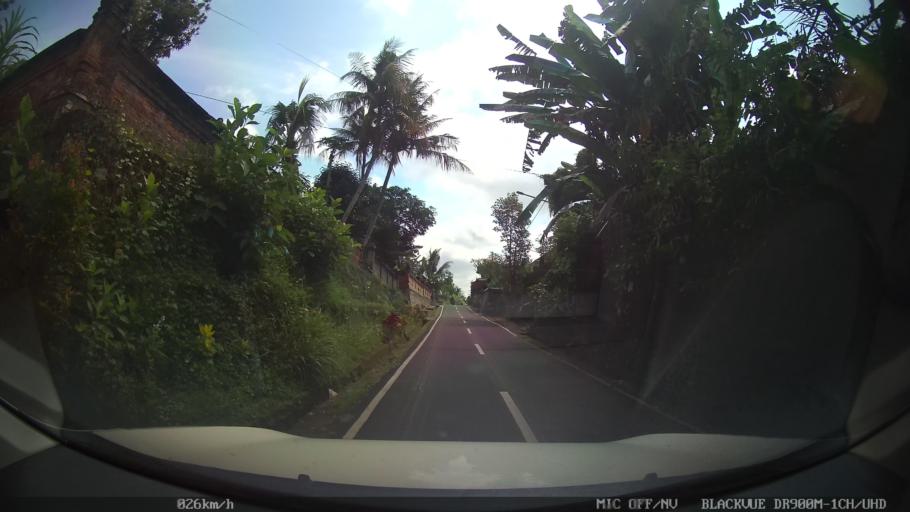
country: ID
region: Bali
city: Banjar Pesalakan
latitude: -8.5194
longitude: 115.3054
